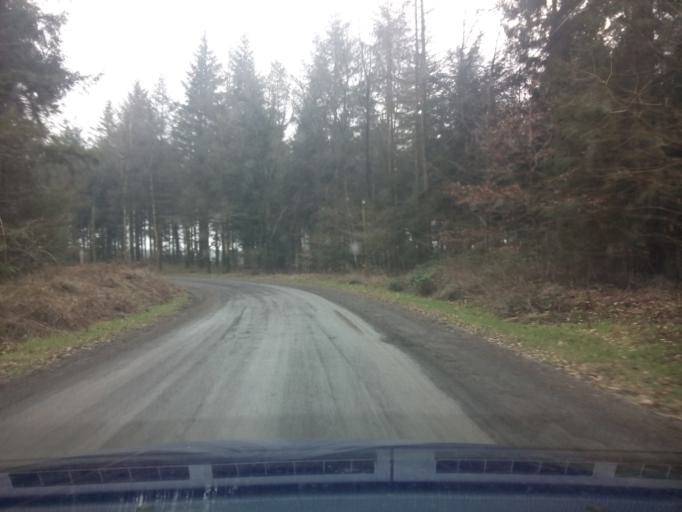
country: DE
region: Lower Saxony
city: Drangstedt
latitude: 53.6150
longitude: 8.7269
